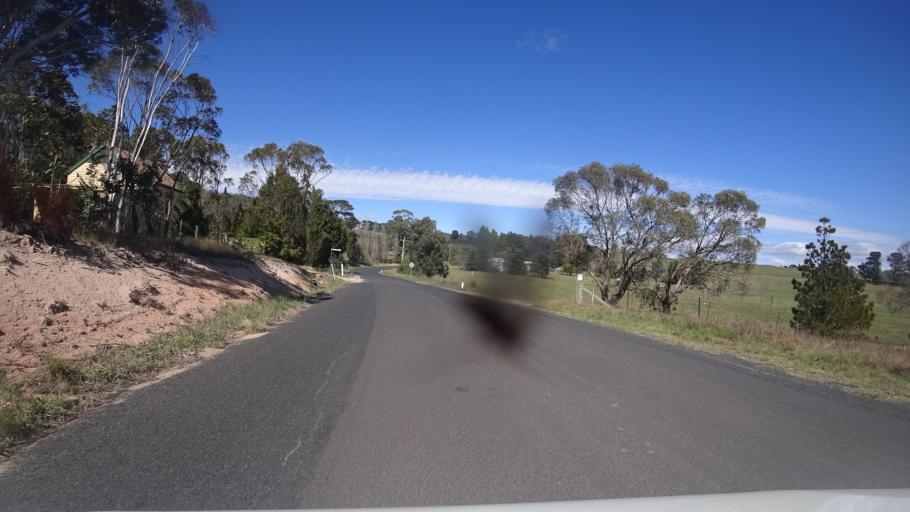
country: AU
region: New South Wales
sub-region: Lithgow
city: Bowenfels
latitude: -33.5157
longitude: 149.9944
